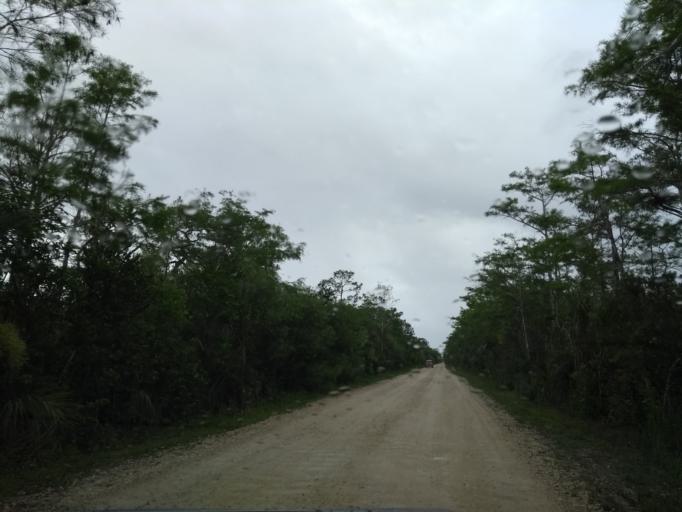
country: US
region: Florida
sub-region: Miami-Dade County
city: The Hammocks
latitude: 25.7605
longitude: -81.0002
